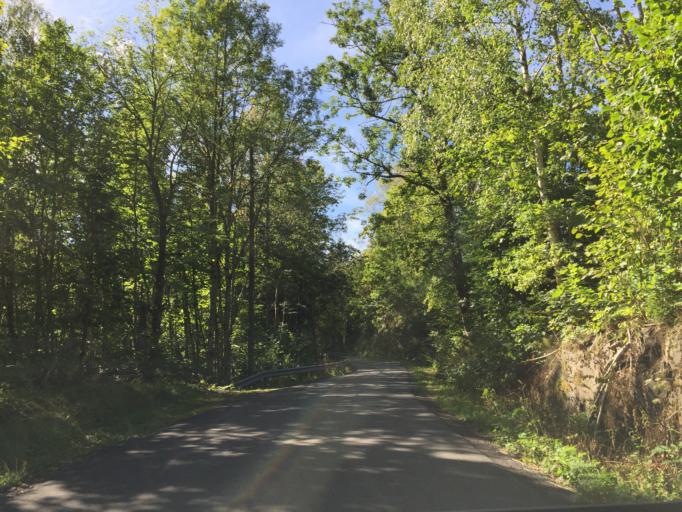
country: NO
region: Vestfold
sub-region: Hof
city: Hof
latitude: 59.4849
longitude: 10.1511
